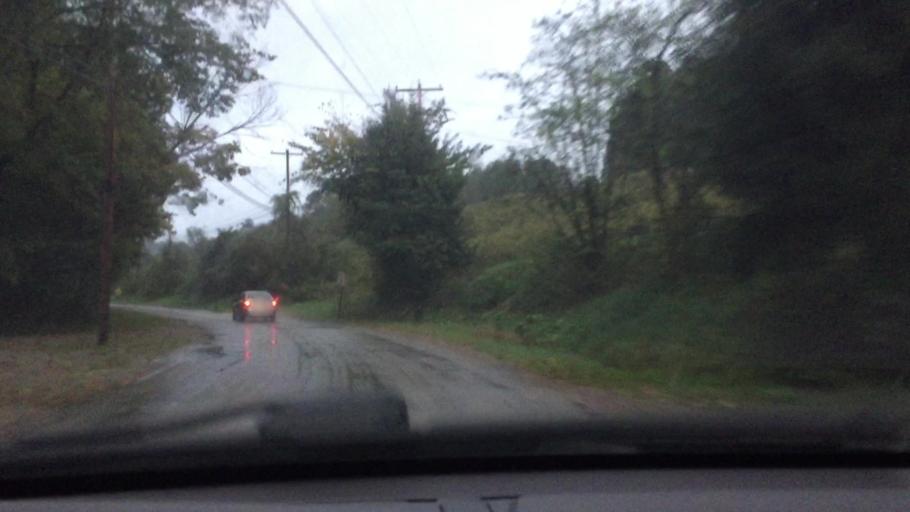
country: US
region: Pennsylvania
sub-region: Washington County
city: Bentleyville
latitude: 40.1294
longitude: -79.9777
